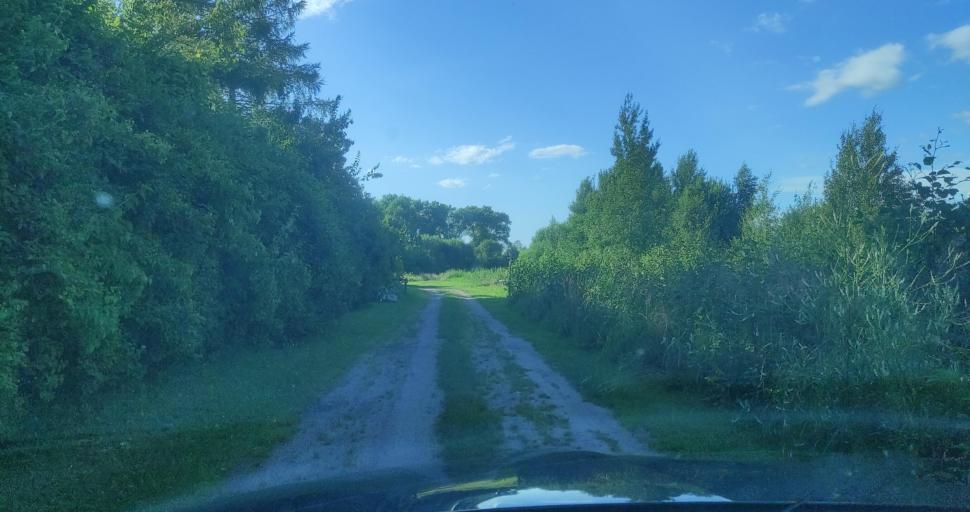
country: LV
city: Tireli
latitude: 56.7044
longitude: 23.4589
